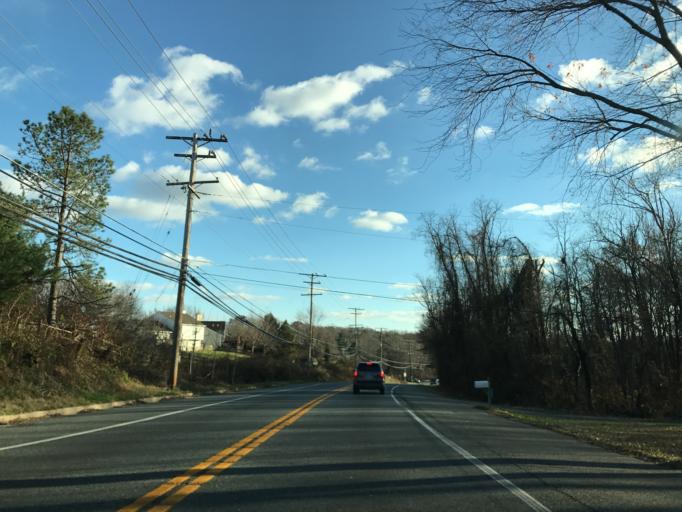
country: US
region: Maryland
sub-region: Harford County
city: Edgewood
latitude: 39.4249
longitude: -76.3293
